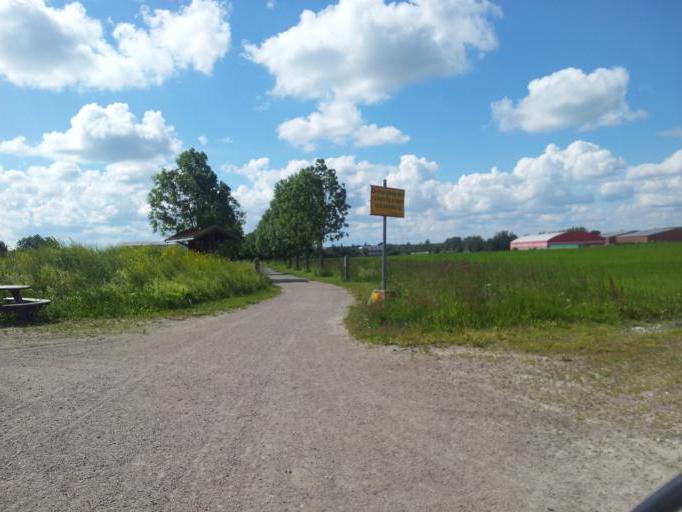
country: SE
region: Uppsala
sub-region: Uppsala Kommun
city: Uppsala
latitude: 59.8799
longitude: 17.6678
